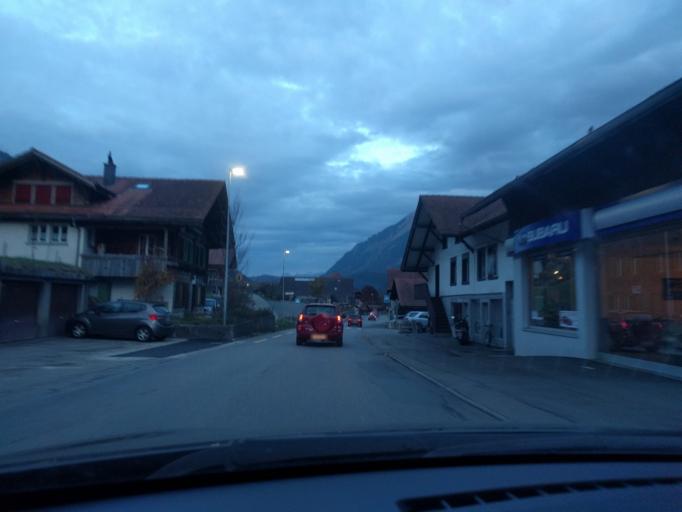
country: CH
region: Bern
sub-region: Frutigen-Niedersimmental District
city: Erlenbach im Simmental
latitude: 46.6602
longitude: 7.5488
